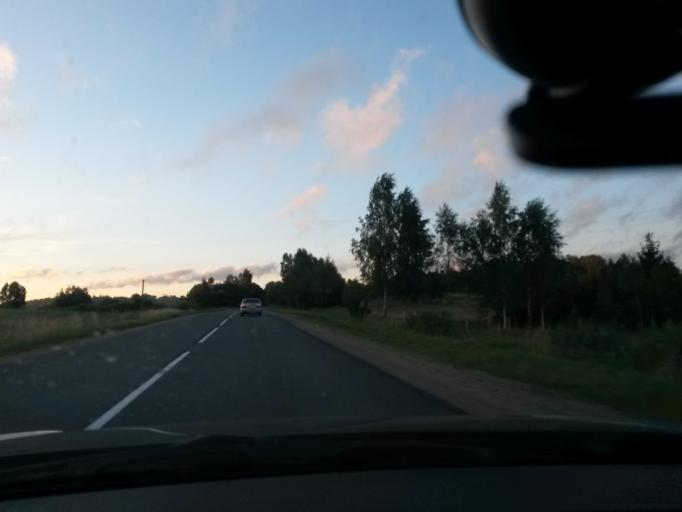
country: LV
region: Madonas Rajons
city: Madona
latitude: 56.7928
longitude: 26.0302
